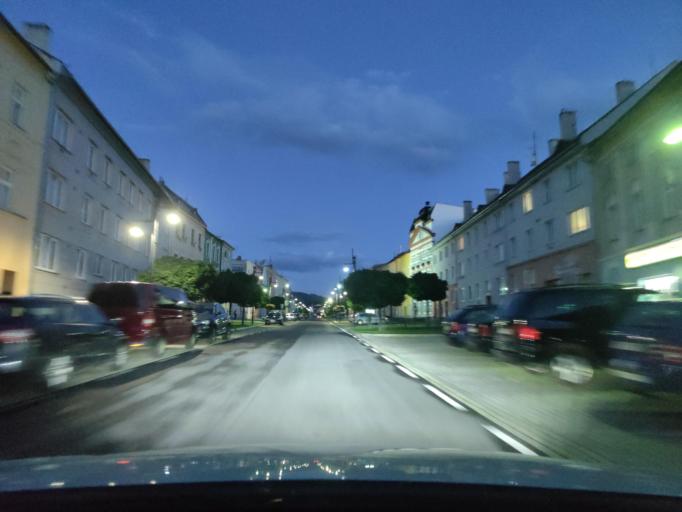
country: CZ
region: Olomoucky
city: Zlate Hory
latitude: 50.2648
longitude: 17.3957
